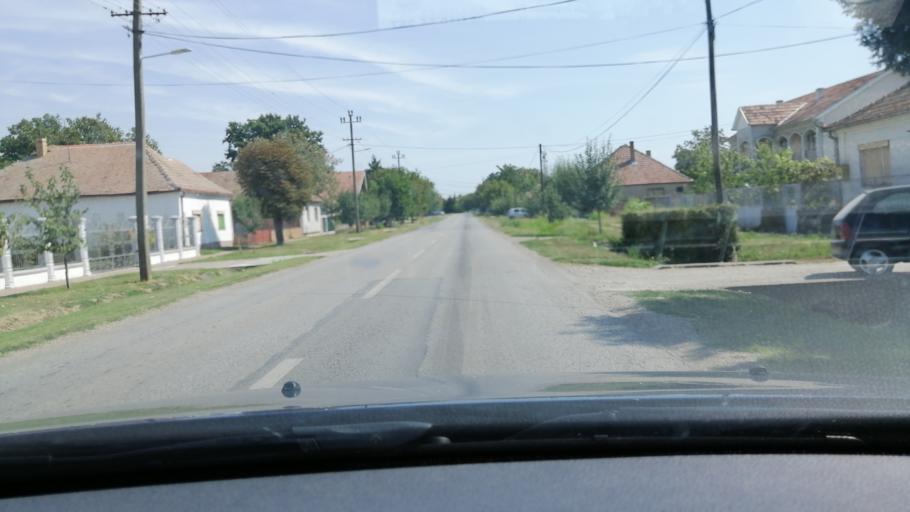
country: RS
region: Autonomna Pokrajina Vojvodina
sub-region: Srednjebanatski Okrug
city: Secanj
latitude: 45.3681
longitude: 20.7632
